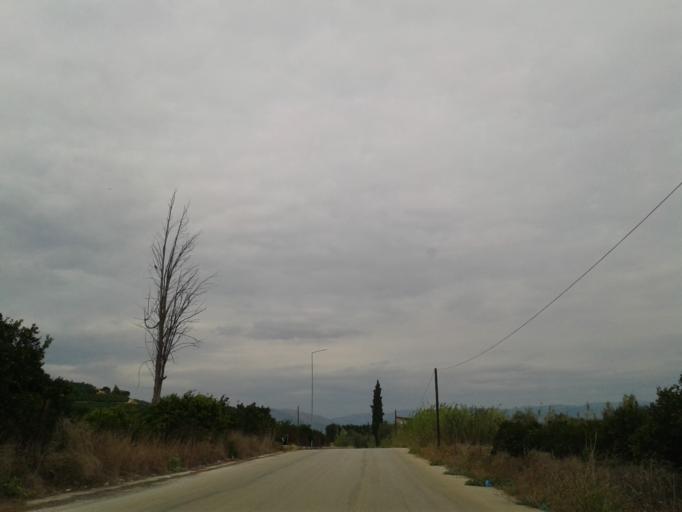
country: GR
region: Peloponnese
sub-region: Nomos Argolidos
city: Argos
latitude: 37.6120
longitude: 22.7047
